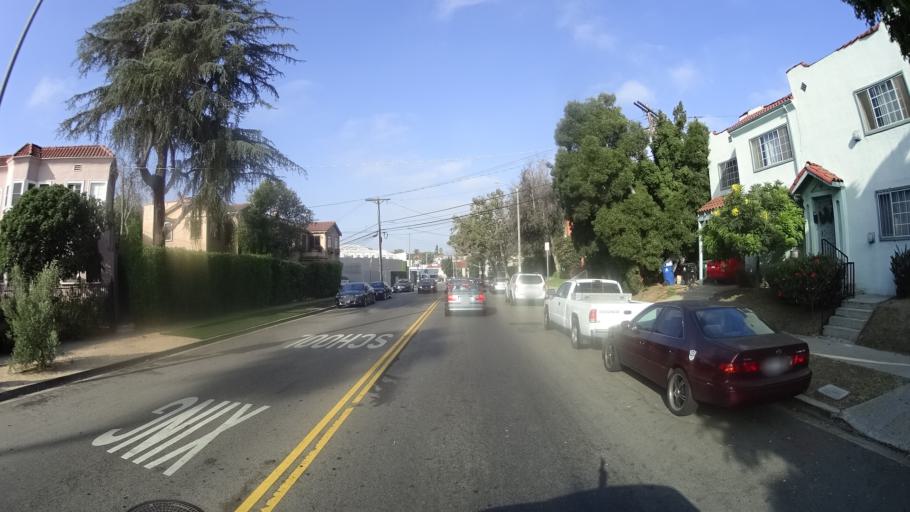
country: US
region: California
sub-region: Los Angeles County
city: West Hollywood
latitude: 34.0550
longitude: -118.3422
